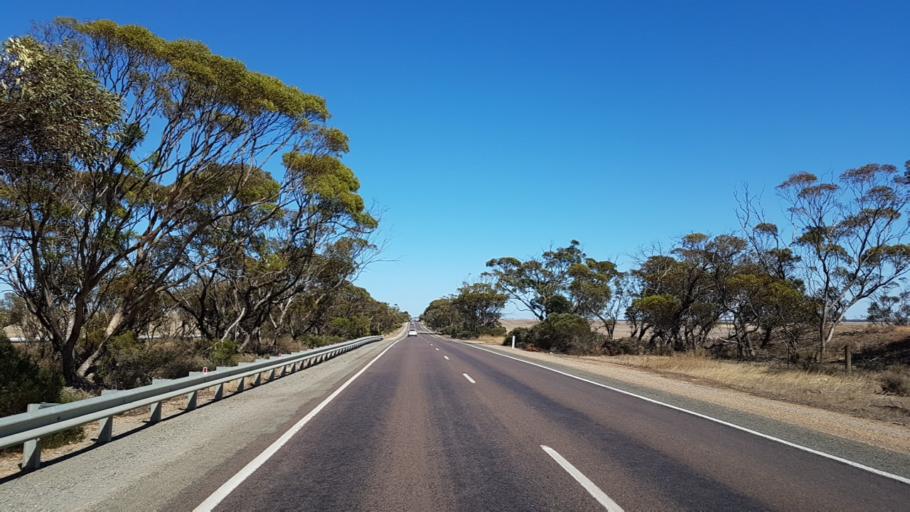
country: AU
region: South Australia
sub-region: Copper Coast
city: Kadina
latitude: -34.0561
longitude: 138.0147
